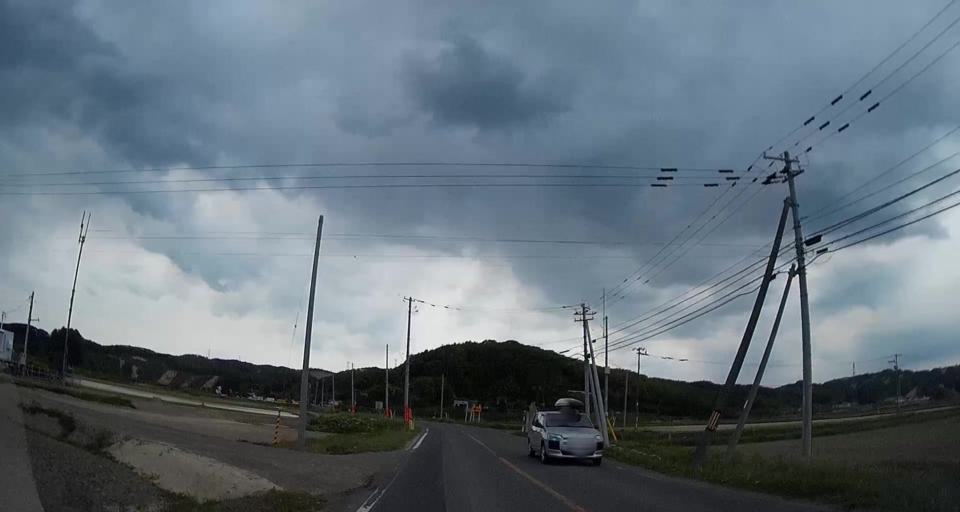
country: JP
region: Hokkaido
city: Chitose
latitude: 42.7576
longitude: 141.9297
